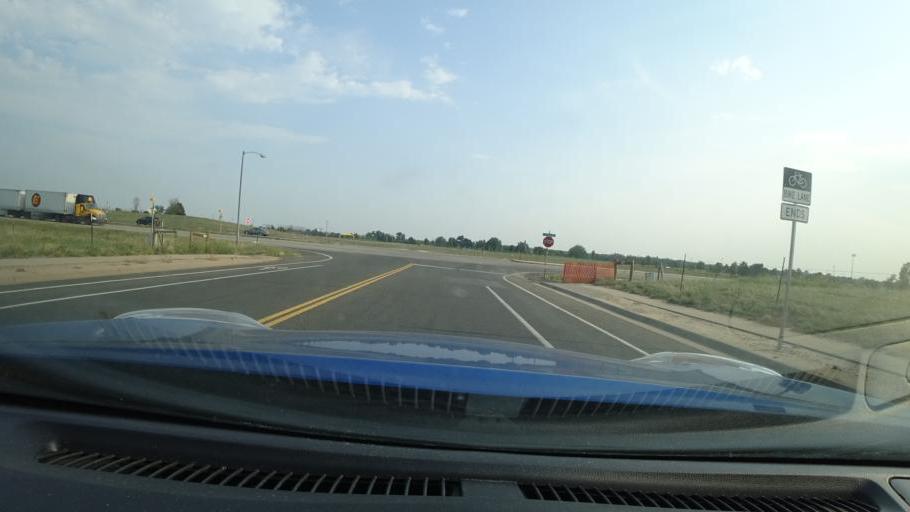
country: US
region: Colorado
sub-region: Adams County
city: Aurora
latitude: 39.7407
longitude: -104.7608
